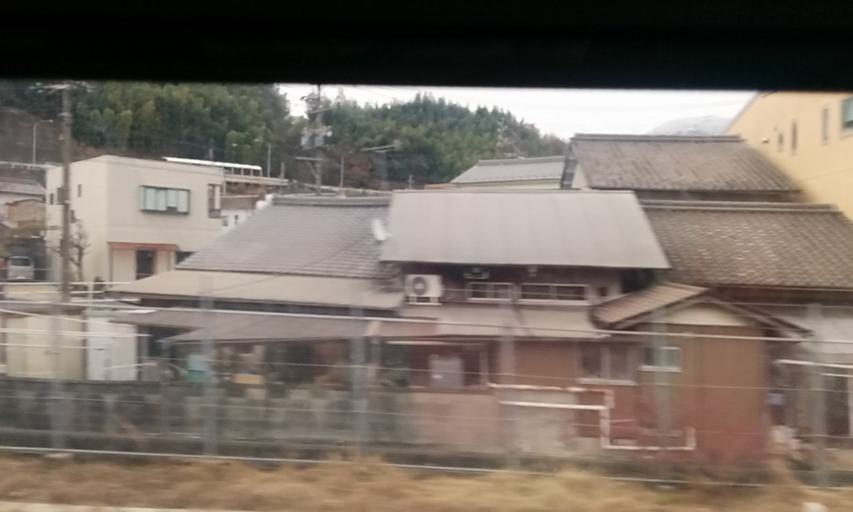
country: JP
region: Gifu
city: Nakatsugawa
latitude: 35.5022
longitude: 137.5037
